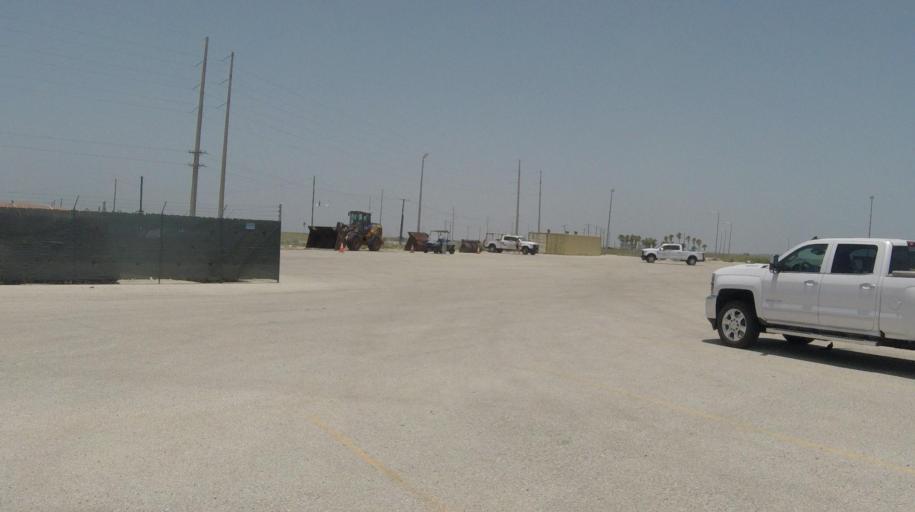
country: US
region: Texas
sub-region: Nueces County
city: Corpus Christi
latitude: 27.6185
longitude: -97.2123
